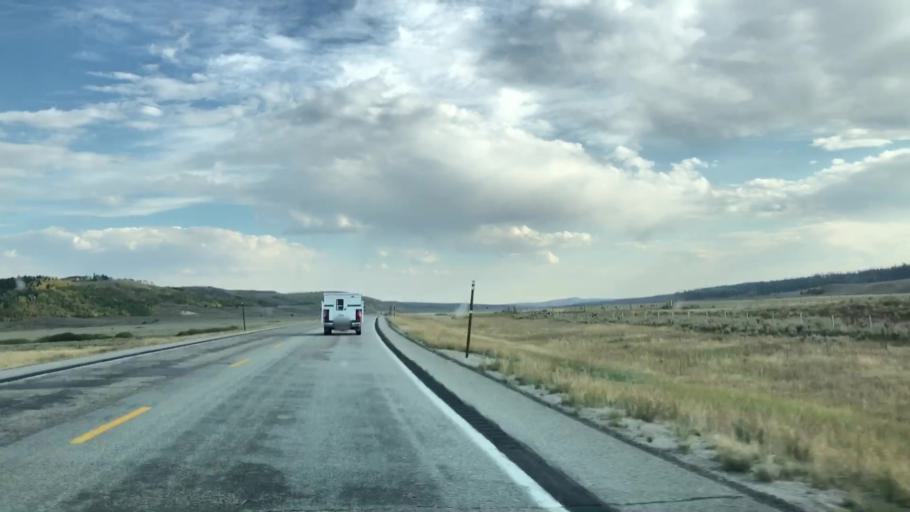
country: US
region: Wyoming
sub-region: Sublette County
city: Pinedale
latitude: 43.1136
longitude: -110.1749
